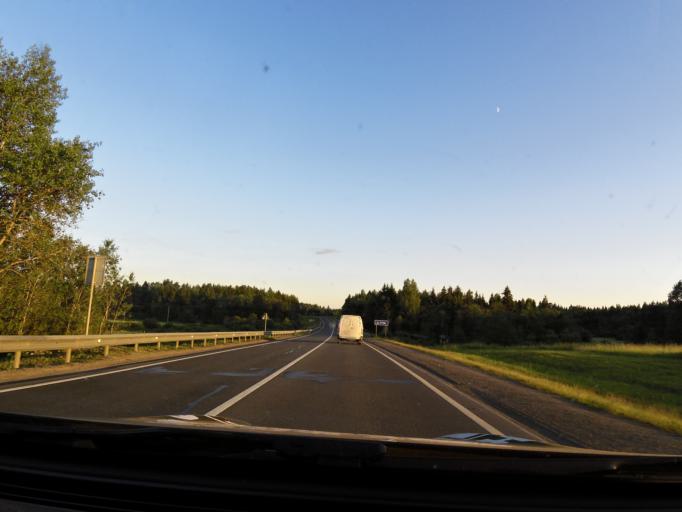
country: RU
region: Jaroslavl
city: Prechistoye
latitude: 58.4832
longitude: 40.3243
